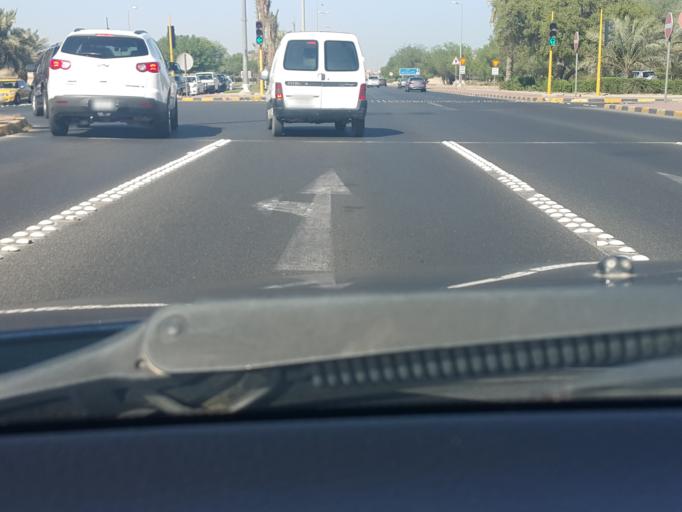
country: KW
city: Bayan
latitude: 29.2799
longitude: 48.0356
